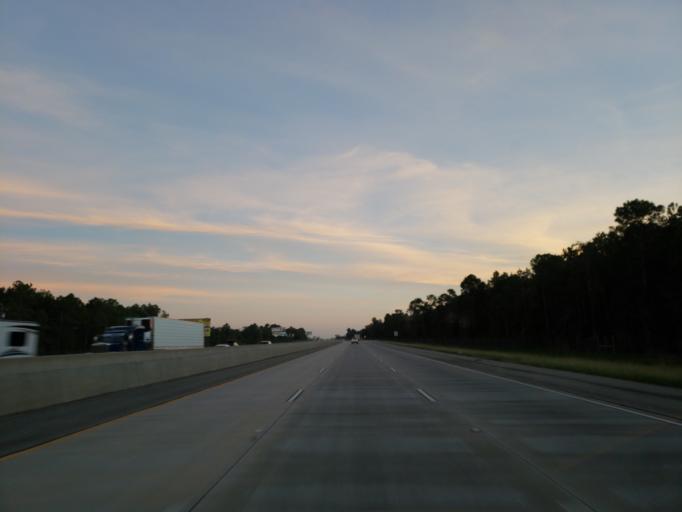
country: US
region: Georgia
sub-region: Cook County
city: Sparks
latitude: 31.2083
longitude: -83.4590
